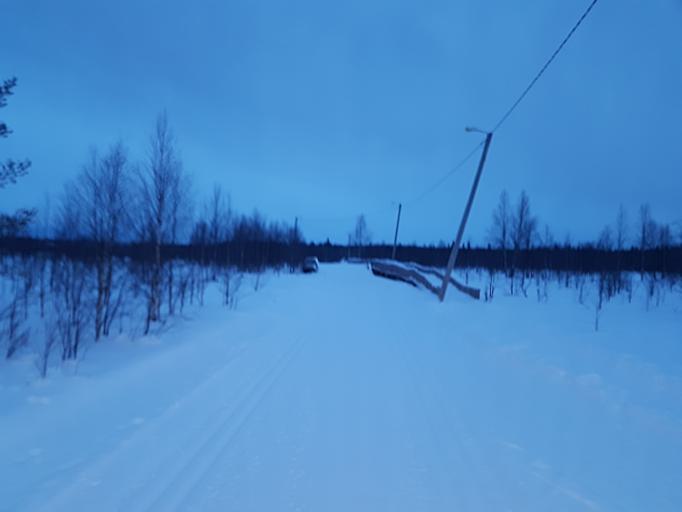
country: FI
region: Lapland
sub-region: Tunturi-Lappi
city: Kolari
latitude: 67.6131
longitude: 24.1688
